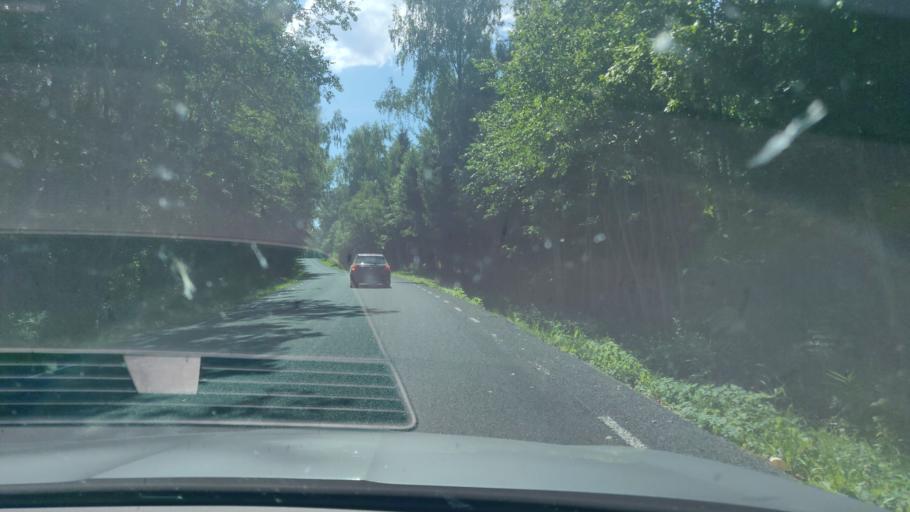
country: EE
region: Tartu
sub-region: Elva linn
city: Elva
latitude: 58.1548
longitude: 26.4701
